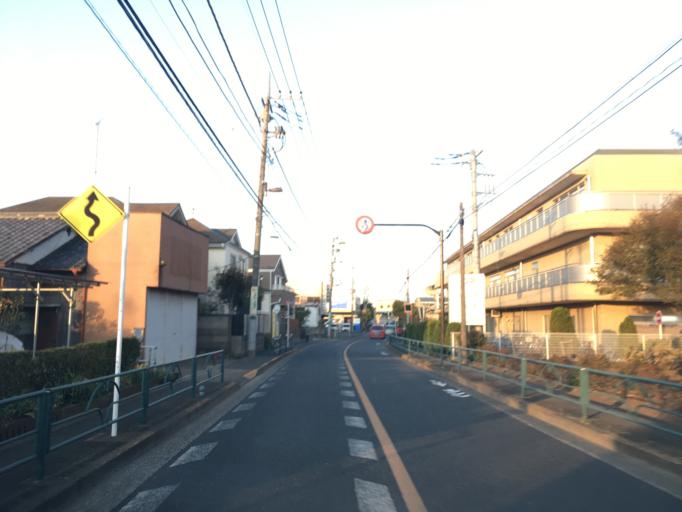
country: JP
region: Tokyo
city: Kokubunji
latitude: 35.7066
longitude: 139.4581
